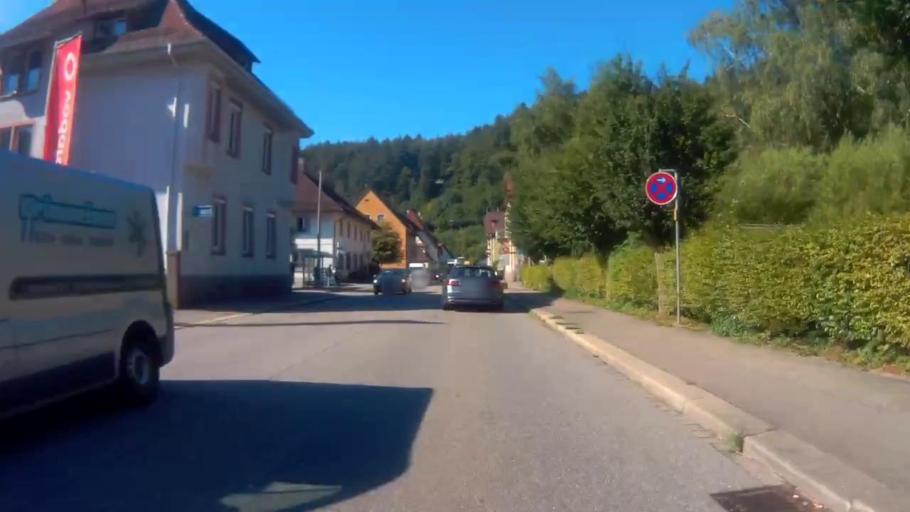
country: DE
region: Baden-Wuerttemberg
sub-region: Freiburg Region
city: Schonau im Schwarzwald
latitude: 47.7854
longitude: 7.8937
